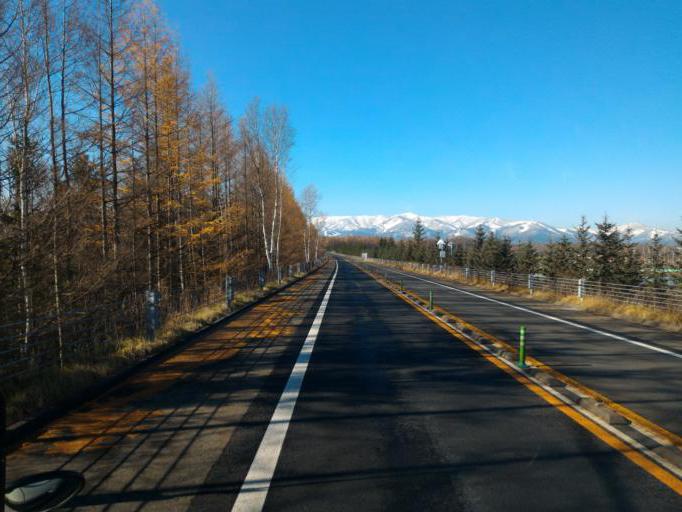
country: JP
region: Hokkaido
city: Otofuke
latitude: 42.9786
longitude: 142.9449
